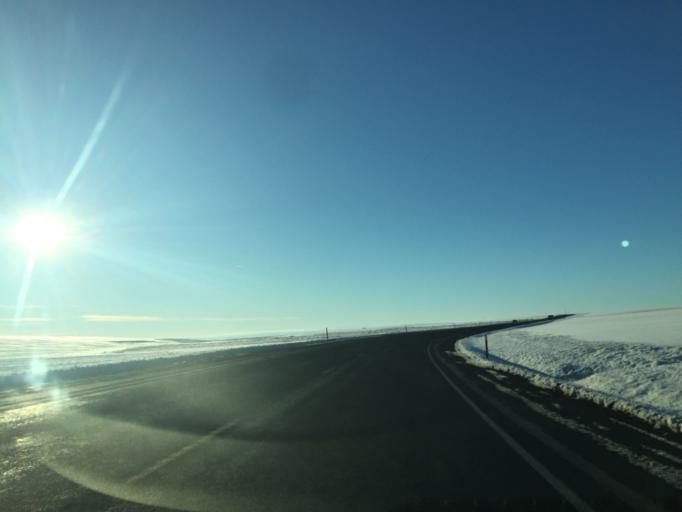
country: US
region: Washington
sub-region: Okanogan County
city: Coulee Dam
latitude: 47.6848
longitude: -118.9860
